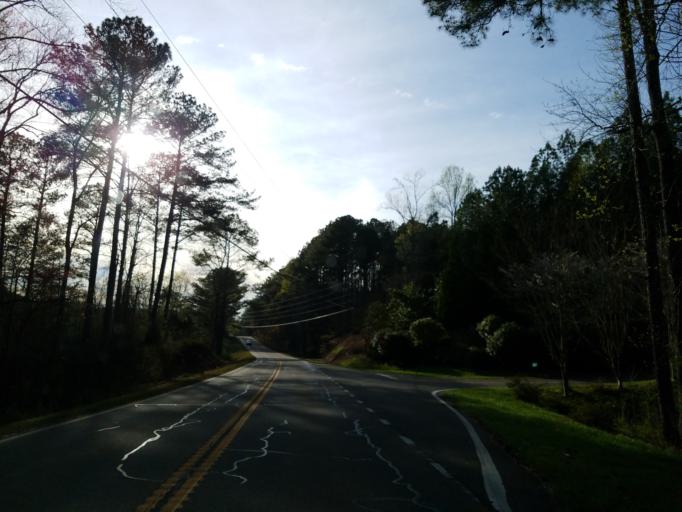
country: US
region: Georgia
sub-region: Pickens County
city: Jasper
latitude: 34.5126
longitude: -84.4484
